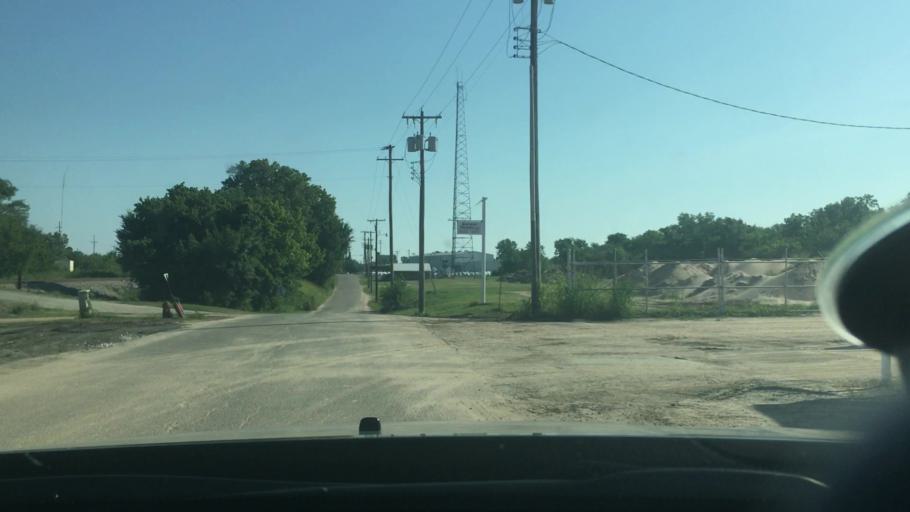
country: US
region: Oklahoma
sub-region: Bryan County
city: Durant
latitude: 33.9866
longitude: -96.3766
